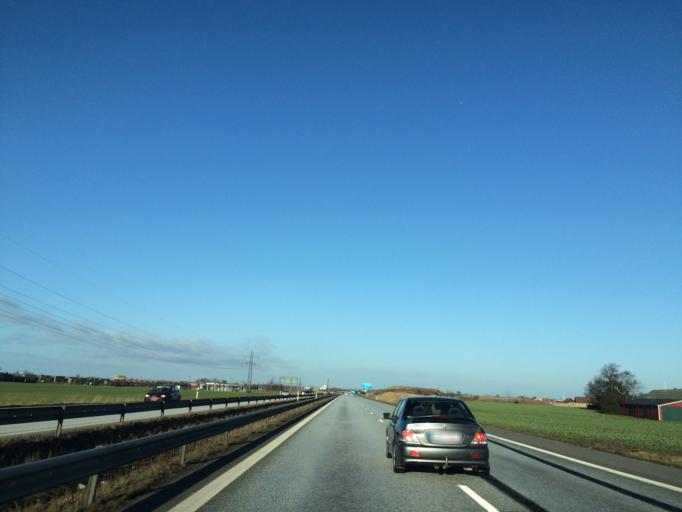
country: SE
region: Skane
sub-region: Lomma Kommun
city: Lomma
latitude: 55.6699
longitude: 13.0996
